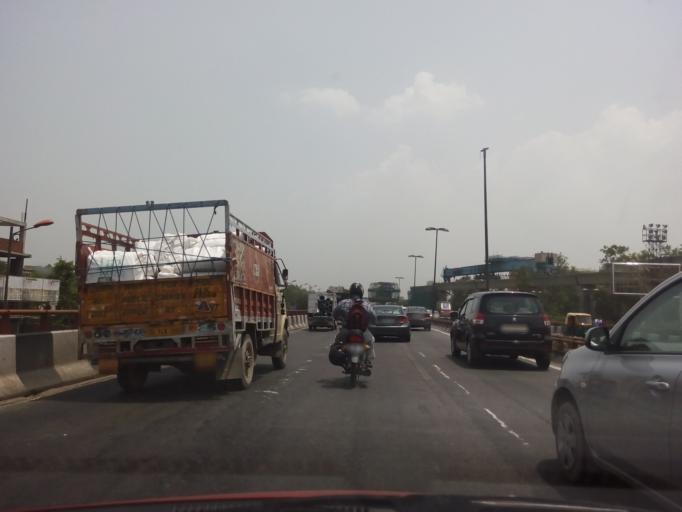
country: IN
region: NCT
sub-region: North West Delhi
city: Pitampura
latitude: 28.6356
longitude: 77.1308
